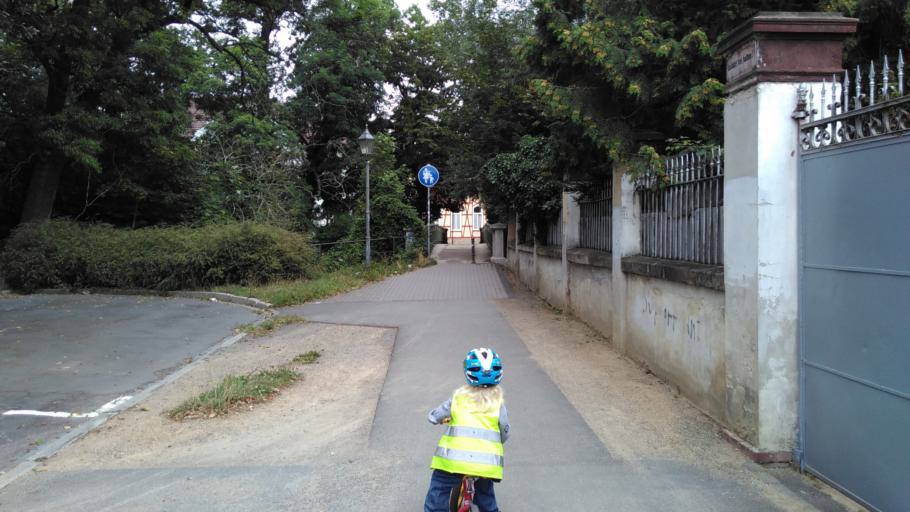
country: DE
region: Saxony-Anhalt
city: Quedlinburg
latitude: 51.7849
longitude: 11.1484
